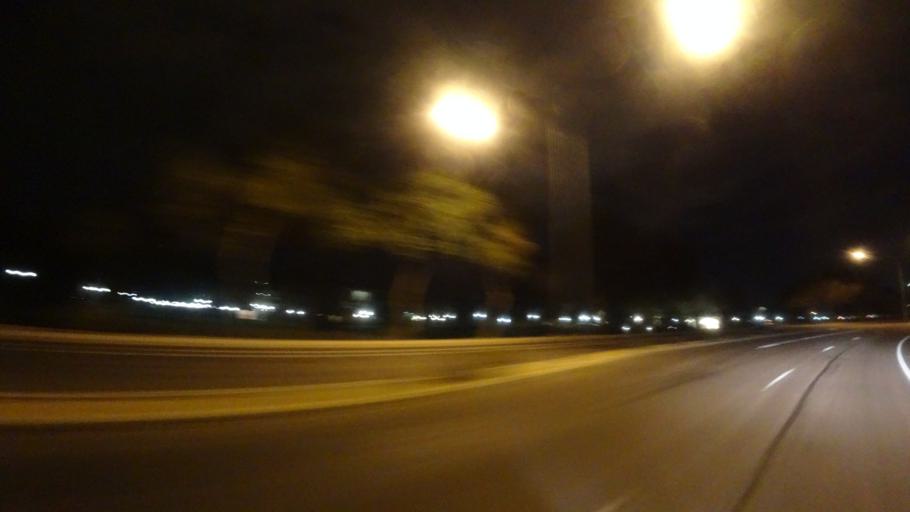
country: US
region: Arizona
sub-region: Maricopa County
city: Gilbert
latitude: 33.3825
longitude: -111.7151
